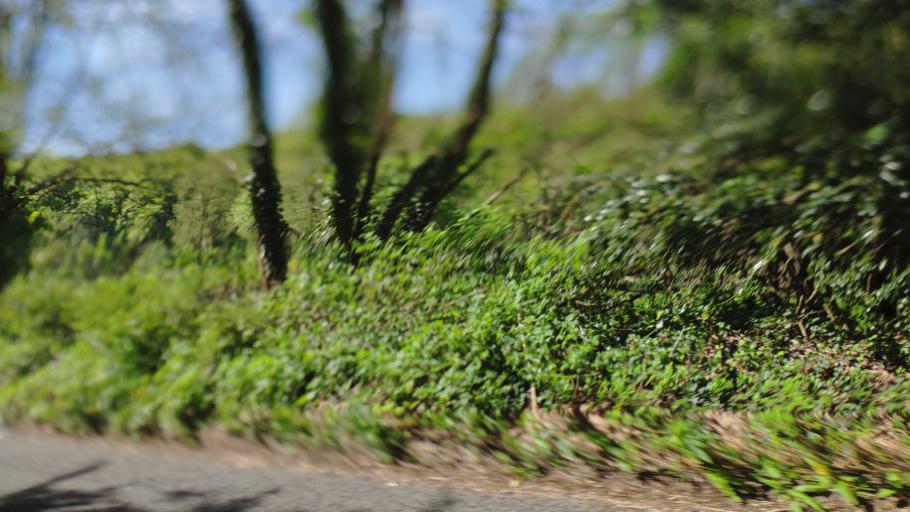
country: IE
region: Munster
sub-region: County Cork
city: Blarney
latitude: 51.9714
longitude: -8.5791
